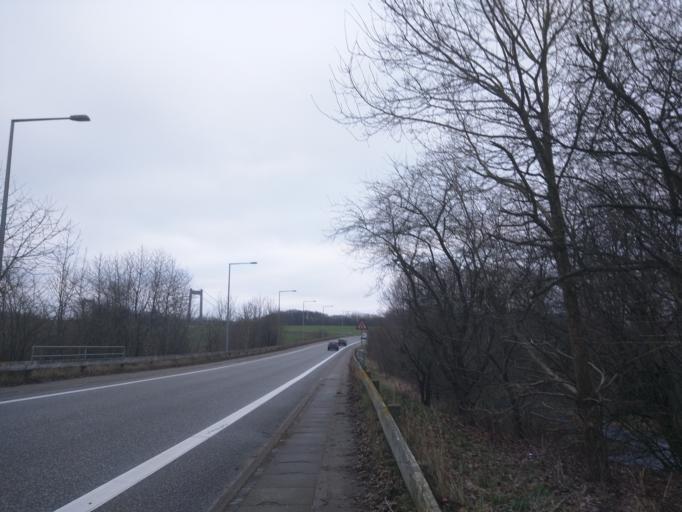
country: DK
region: South Denmark
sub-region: Fredericia Kommune
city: Snoghoj
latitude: 55.5291
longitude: 9.7313
